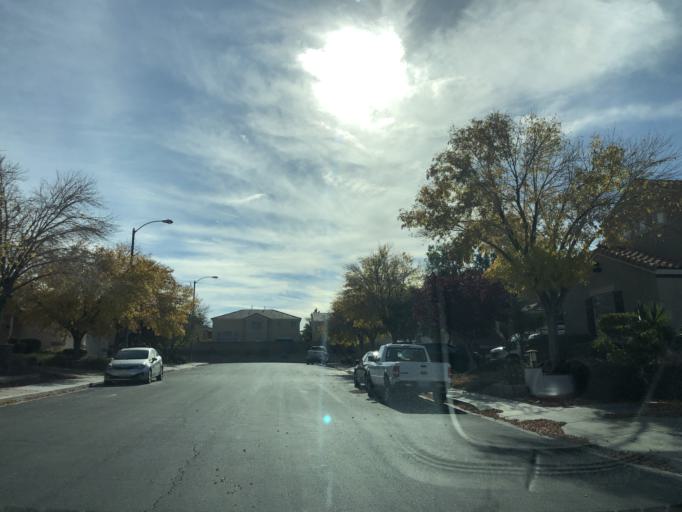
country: US
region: Nevada
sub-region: Clark County
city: Whitney
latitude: 36.0090
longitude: -115.0941
